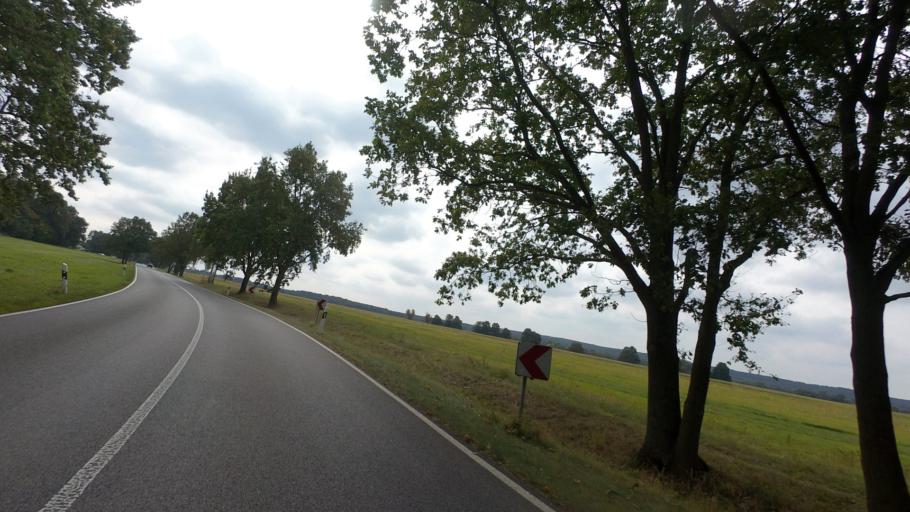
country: DE
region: Brandenburg
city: Luckau
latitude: 51.7839
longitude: 13.6880
